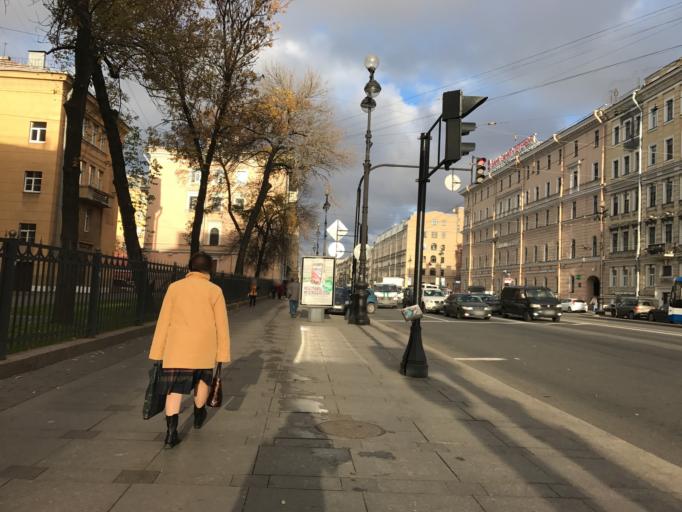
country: RU
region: St.-Petersburg
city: Centralniy
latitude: 59.9245
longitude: 30.3825
